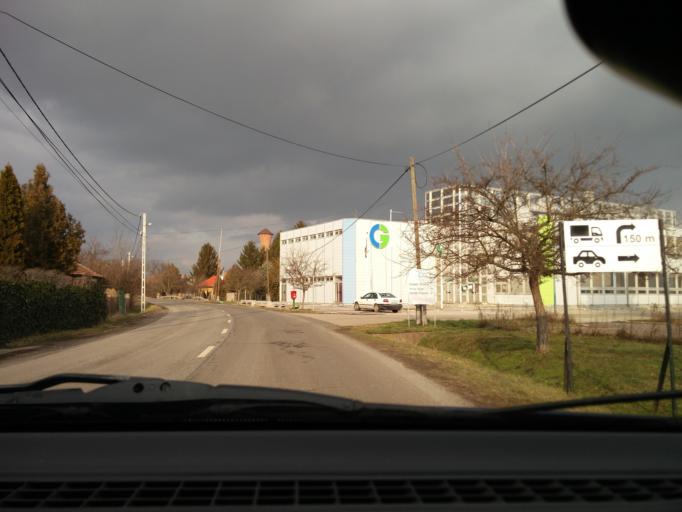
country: HU
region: Pest
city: Tapioszele
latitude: 47.3258
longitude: 19.8806
